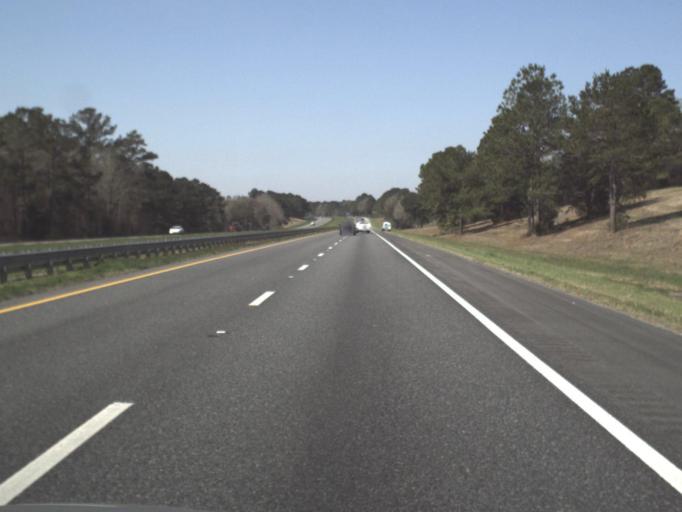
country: US
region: Florida
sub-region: Jackson County
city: Marianna
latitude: 30.7581
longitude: -85.3044
